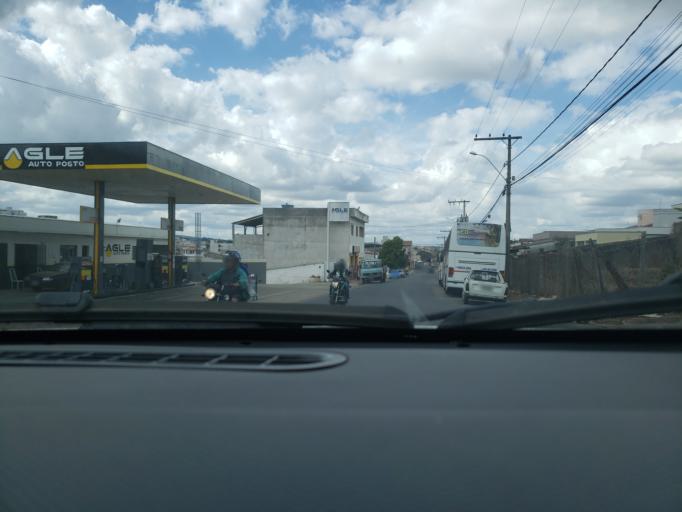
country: BR
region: Minas Gerais
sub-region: Campo Belo
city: Campo Belo
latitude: -20.9050
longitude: -45.2802
